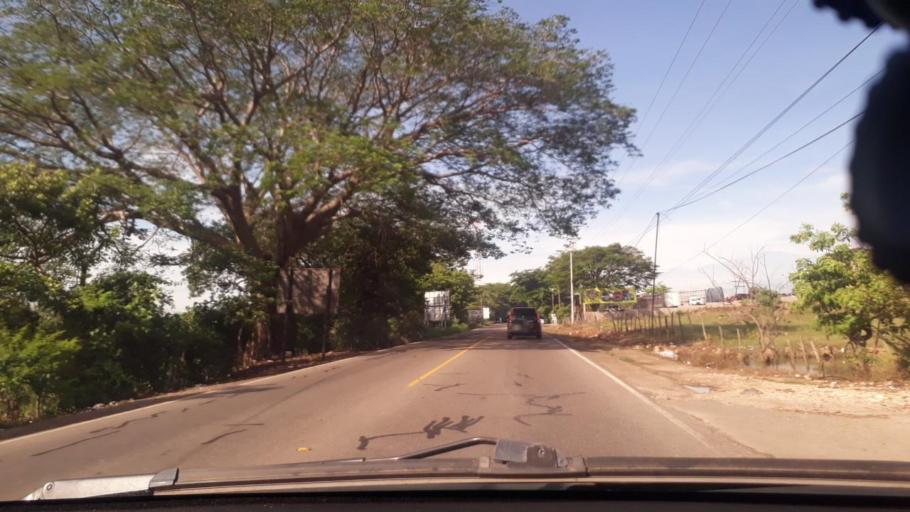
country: GT
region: Jutiapa
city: El Progreso
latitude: 14.3226
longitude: -89.8623
